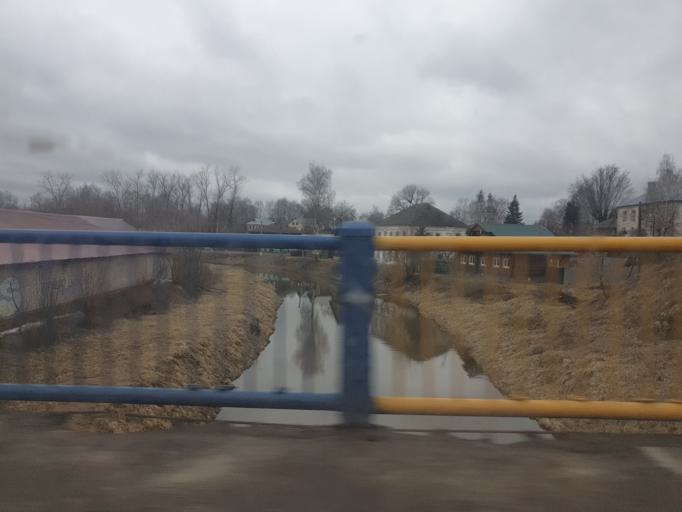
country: RU
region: Kostroma
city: Nerekhta
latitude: 57.4627
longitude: 40.5726
